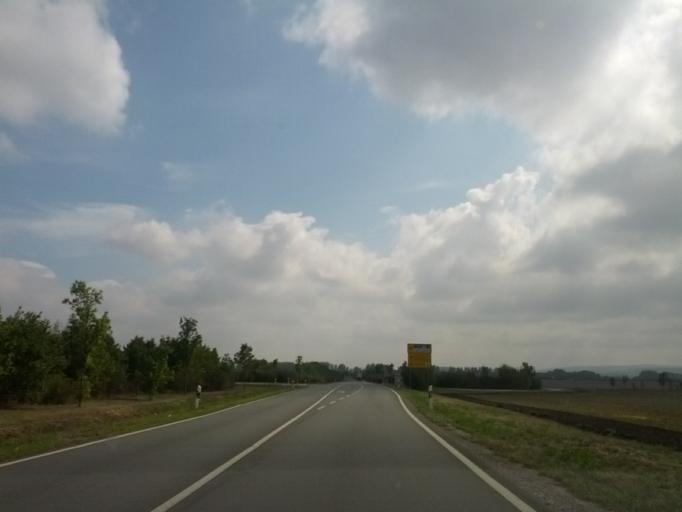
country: DE
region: Thuringia
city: Apfelstadt
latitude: 50.8988
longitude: 10.8778
